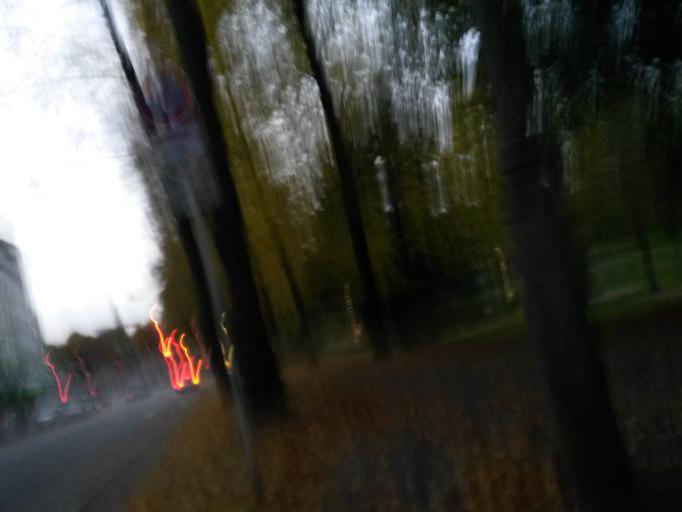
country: DE
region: Bremen
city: Bremen
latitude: 53.0780
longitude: 8.8103
